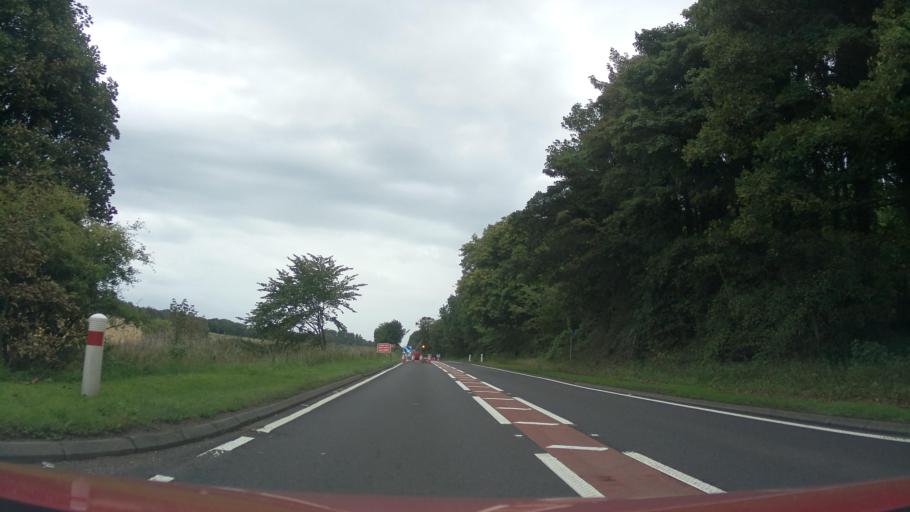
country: GB
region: Scotland
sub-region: Fife
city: Crossford
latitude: 56.0448
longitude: -3.5012
